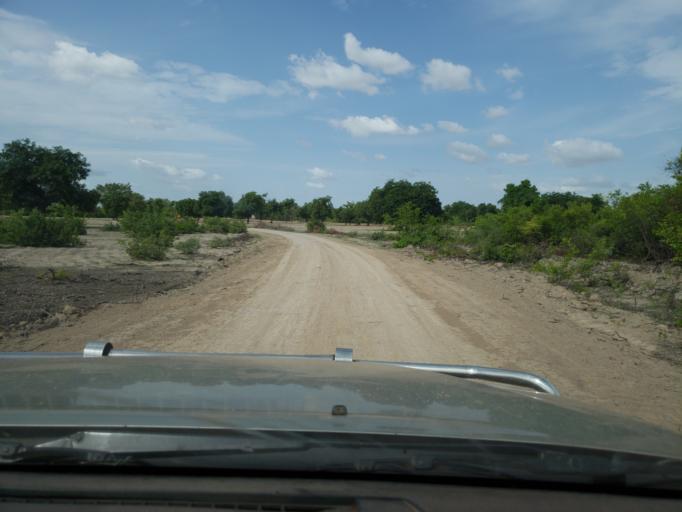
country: ML
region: Segou
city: Bla
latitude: 12.7687
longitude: -5.6186
